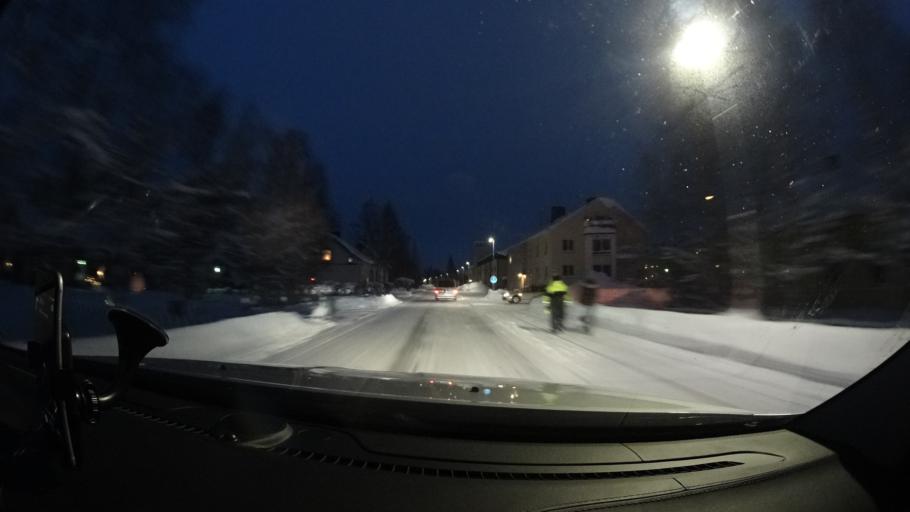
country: SE
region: Norrbotten
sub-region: Gallivare Kommun
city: Malmberget
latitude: 67.6802
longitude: 21.6371
